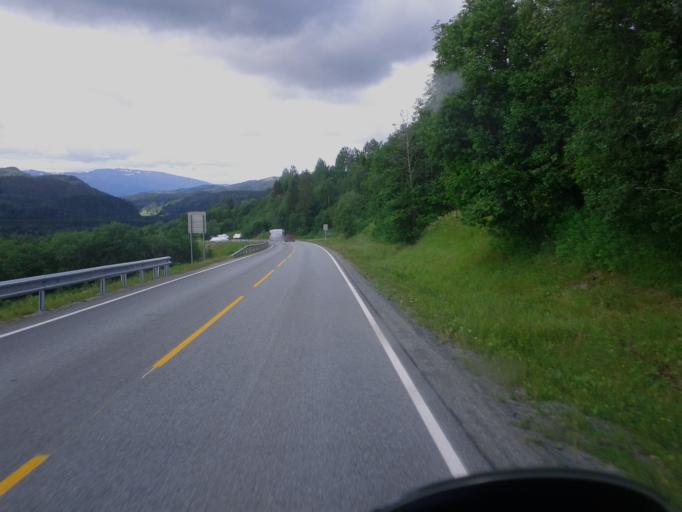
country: NO
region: Nord-Trondelag
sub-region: Grong
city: Grong
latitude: 64.5351
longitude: 12.4140
